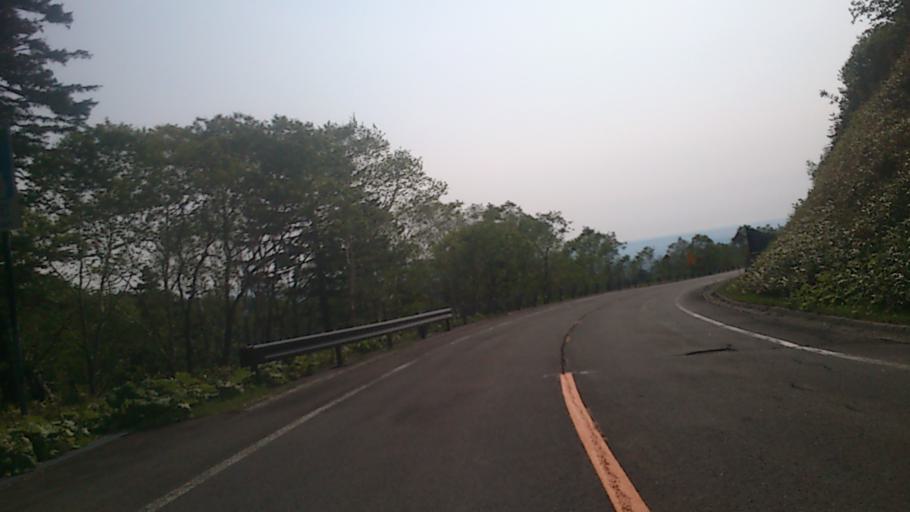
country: JP
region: Hokkaido
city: Bihoro
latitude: 43.4628
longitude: 144.2320
